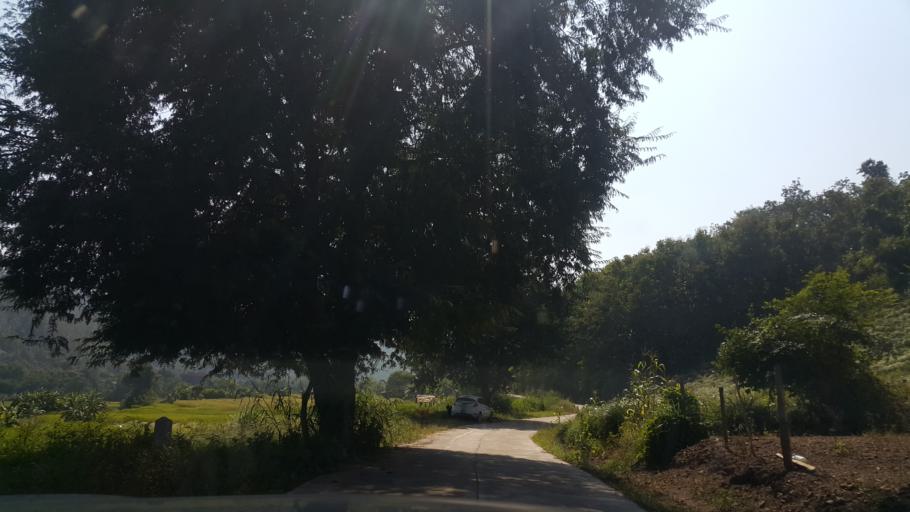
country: TH
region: Chiang Mai
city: Samoeng
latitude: 18.9166
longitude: 98.6060
